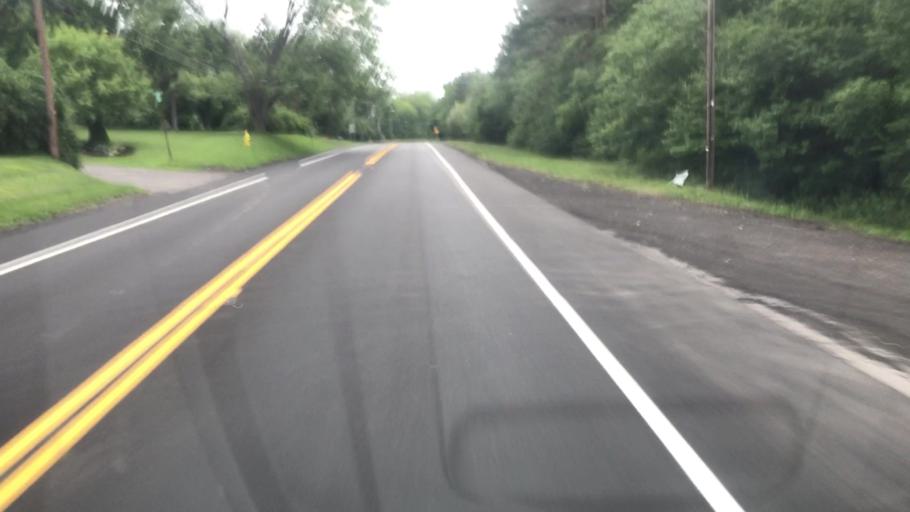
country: US
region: New York
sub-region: Cayuga County
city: Melrose Park
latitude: 42.8986
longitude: -76.5243
